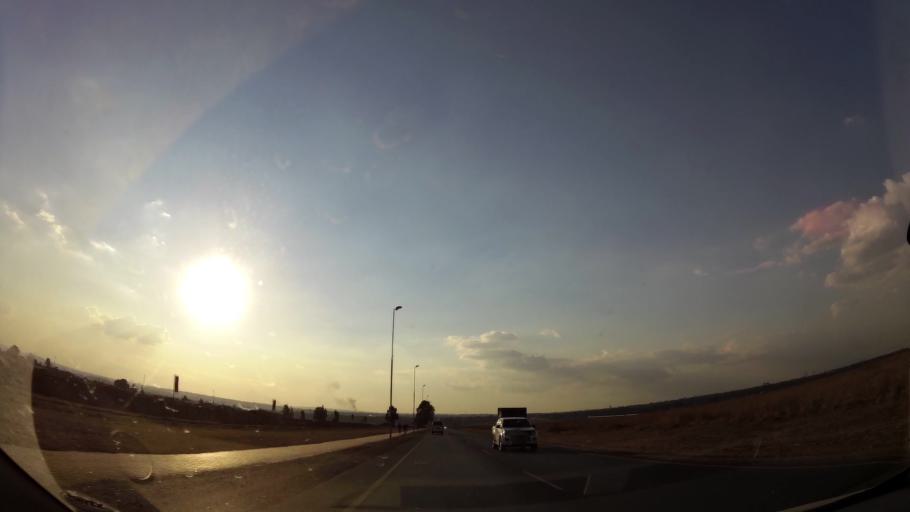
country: ZA
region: Gauteng
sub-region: Ekurhuleni Metropolitan Municipality
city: Boksburg
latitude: -26.2829
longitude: 28.2456
